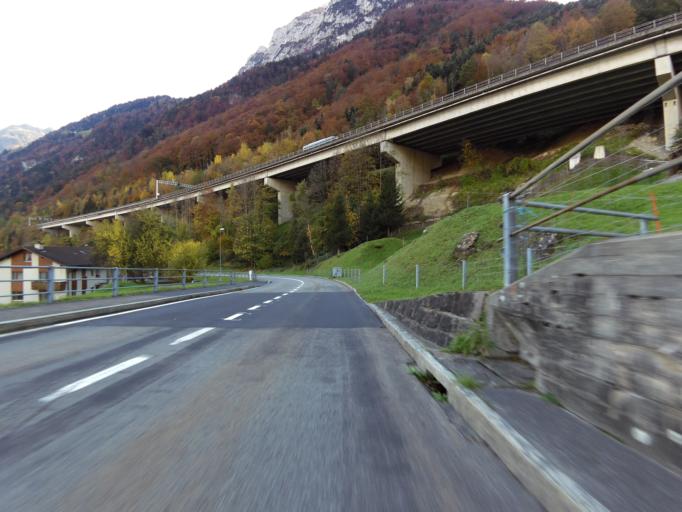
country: CH
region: Uri
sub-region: Uri
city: Flueelen
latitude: 46.8976
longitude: 8.5934
